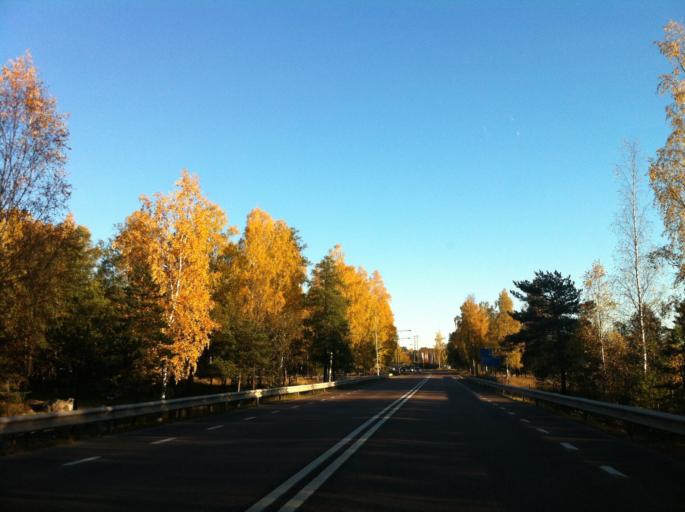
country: SE
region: Dalarna
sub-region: Faluns Kommun
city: Falun
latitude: 60.6279
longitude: 15.6048
